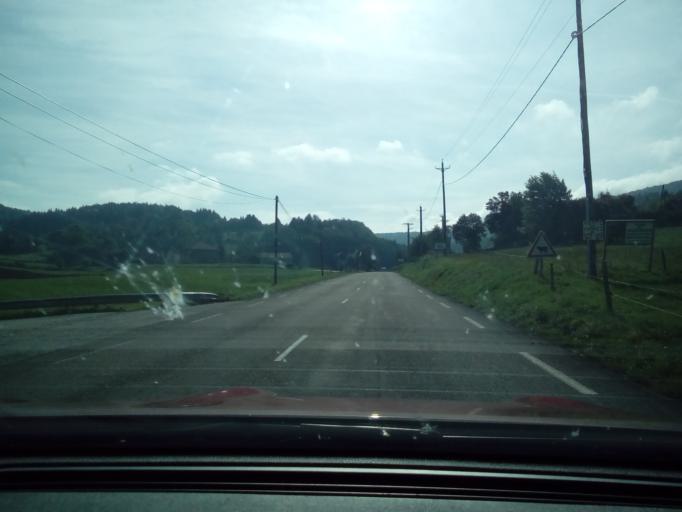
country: FR
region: Rhone-Alpes
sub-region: Departement de la Drome
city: Saint-Laurent-en-Royans
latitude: 44.9949
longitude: 5.4190
